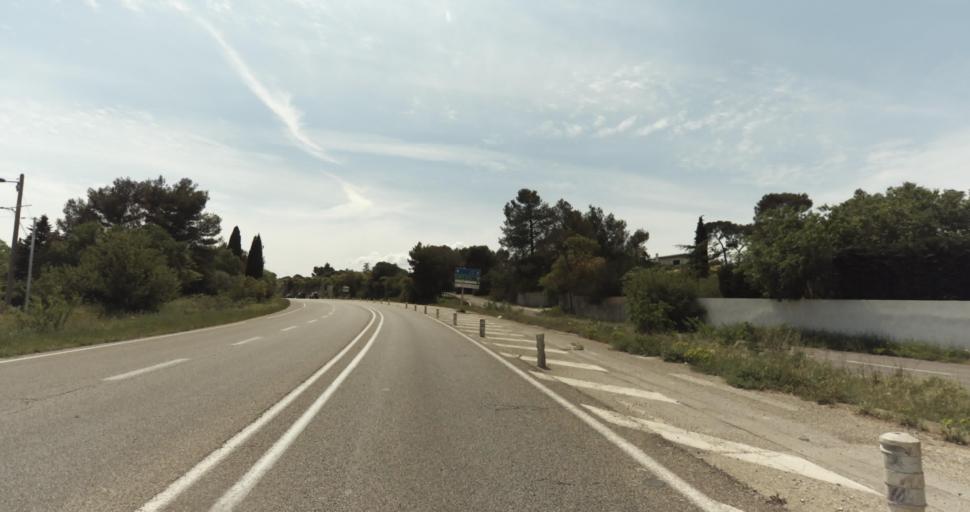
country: FR
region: Languedoc-Roussillon
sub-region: Departement du Gard
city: Nimes
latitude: 43.8444
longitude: 4.3168
